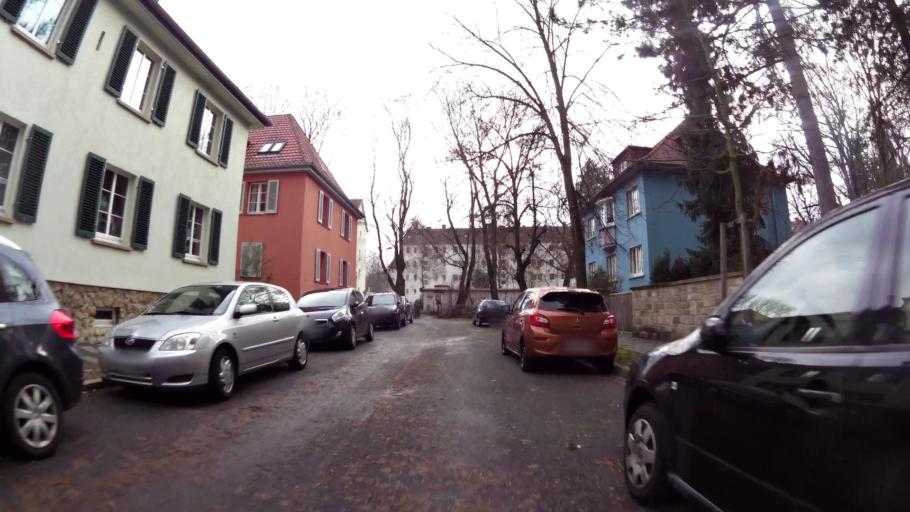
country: DE
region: Thuringia
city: Weimar
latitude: 50.9787
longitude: 11.3111
